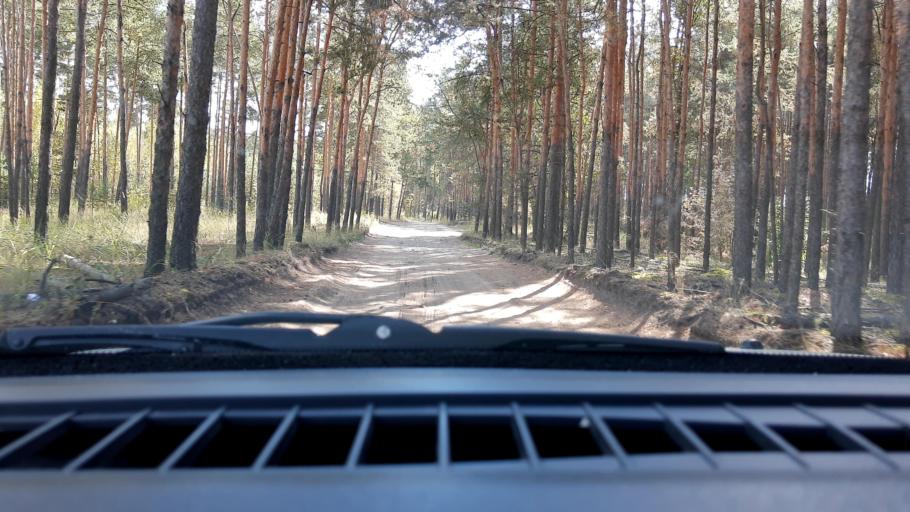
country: RU
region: Nizjnij Novgorod
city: Gorbatovka
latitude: 56.3100
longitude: 43.6989
